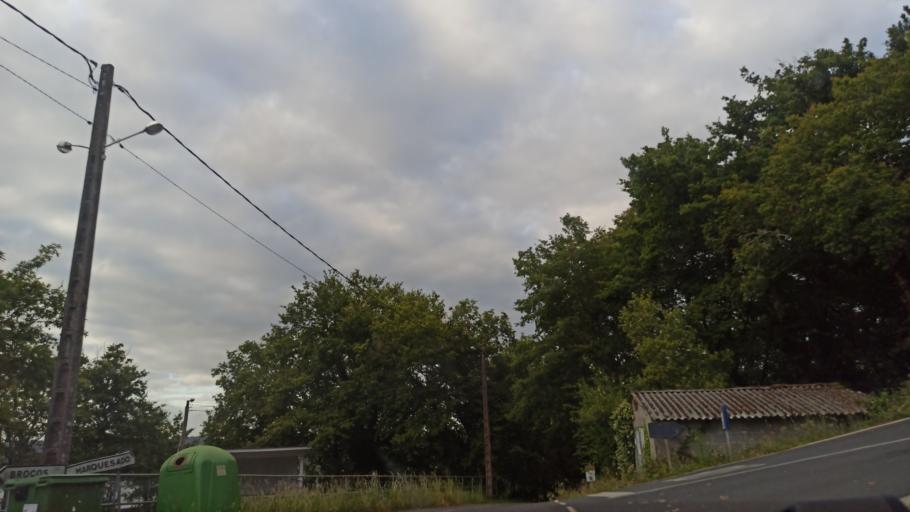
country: ES
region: Galicia
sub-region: Provincia da Coruna
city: Santiso
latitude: 42.8336
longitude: -8.1241
